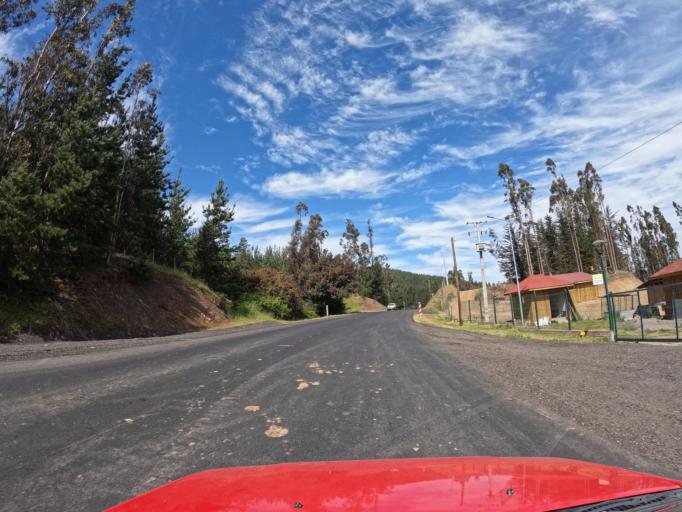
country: CL
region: Maule
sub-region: Provincia de Talca
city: Constitucion
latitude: -35.0436
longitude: -72.0545
